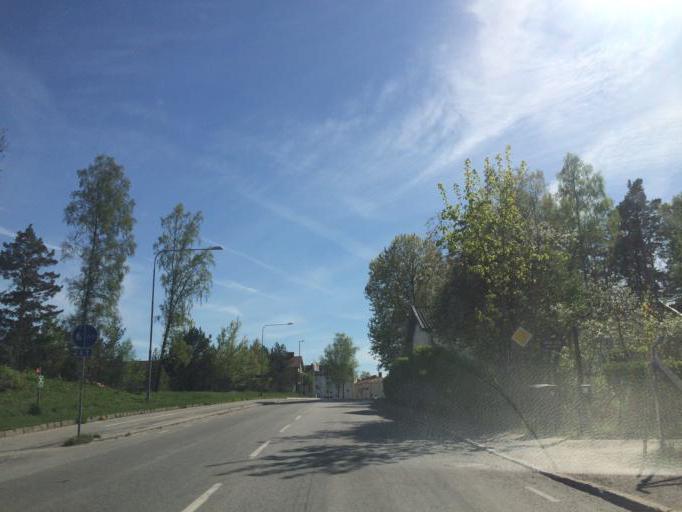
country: SE
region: Soedermanland
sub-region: Katrineholms Kommun
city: Katrineholm
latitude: 58.9940
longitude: 16.1872
